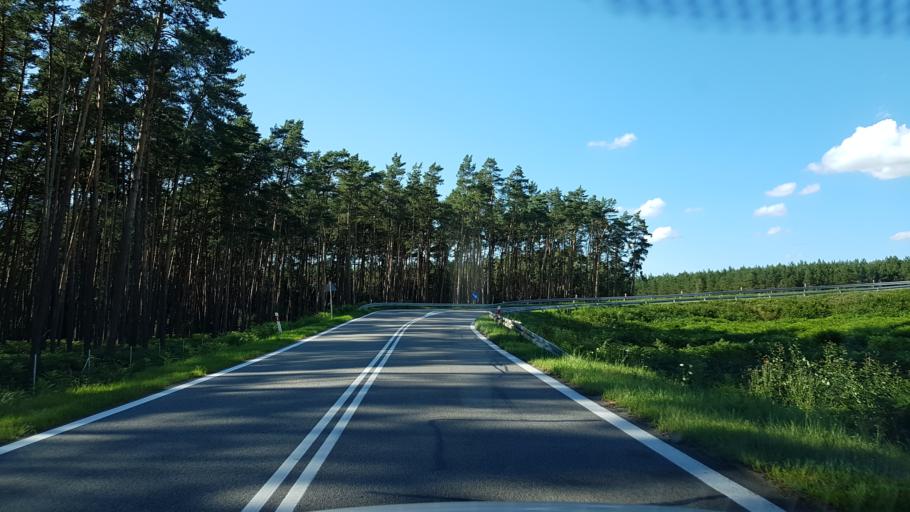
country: PL
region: West Pomeranian Voivodeship
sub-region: Powiat goleniowski
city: Goleniow
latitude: 53.5329
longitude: 14.8093
